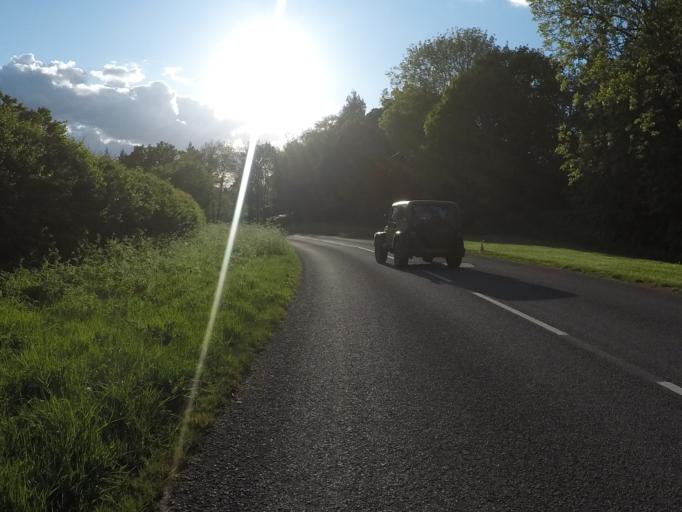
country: GB
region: England
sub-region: Oxfordshire
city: Charlbury
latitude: 51.8682
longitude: -1.4667
